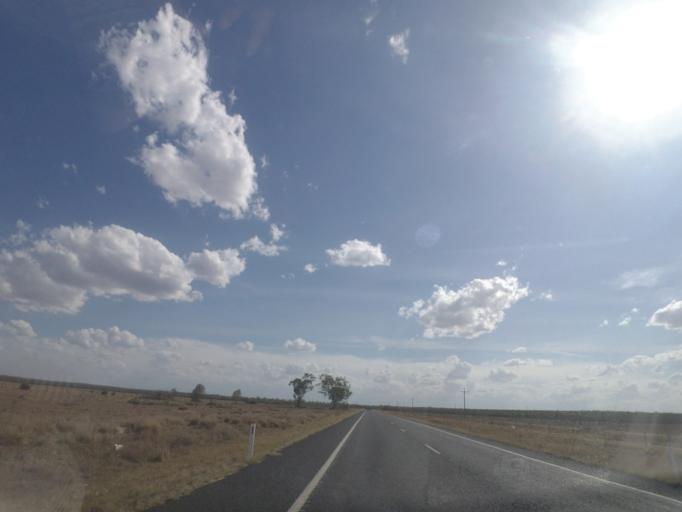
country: AU
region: New South Wales
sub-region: Moree Plains
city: Boggabilla
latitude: -28.5260
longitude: 150.9023
